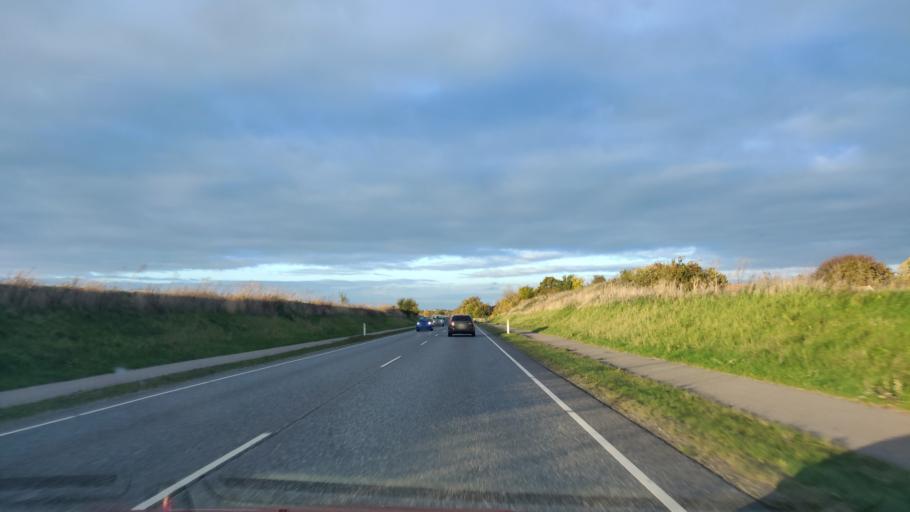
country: DK
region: Zealand
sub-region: Holbaek Kommune
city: Vipperod
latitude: 55.6708
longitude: 11.6890
